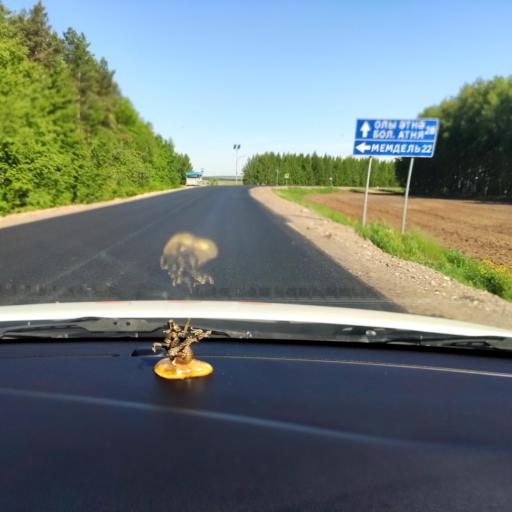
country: RU
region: Tatarstan
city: Vysokaya Gora
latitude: 56.1062
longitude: 49.1784
